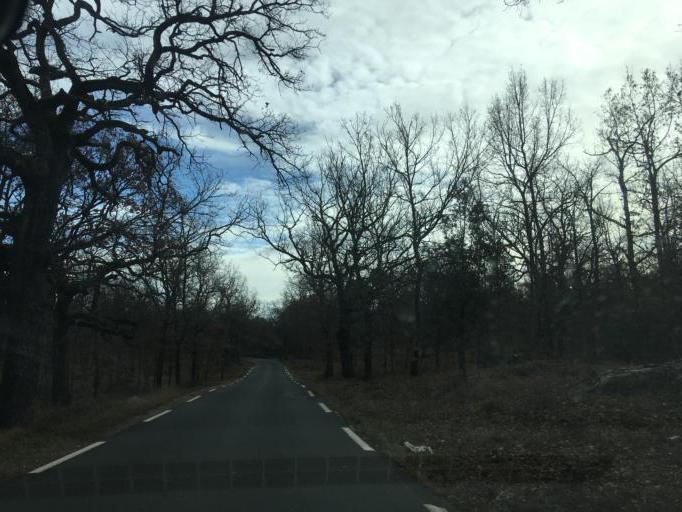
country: FR
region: Provence-Alpes-Cote d'Azur
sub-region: Departement du Var
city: Bras
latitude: 43.4497
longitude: 5.9832
